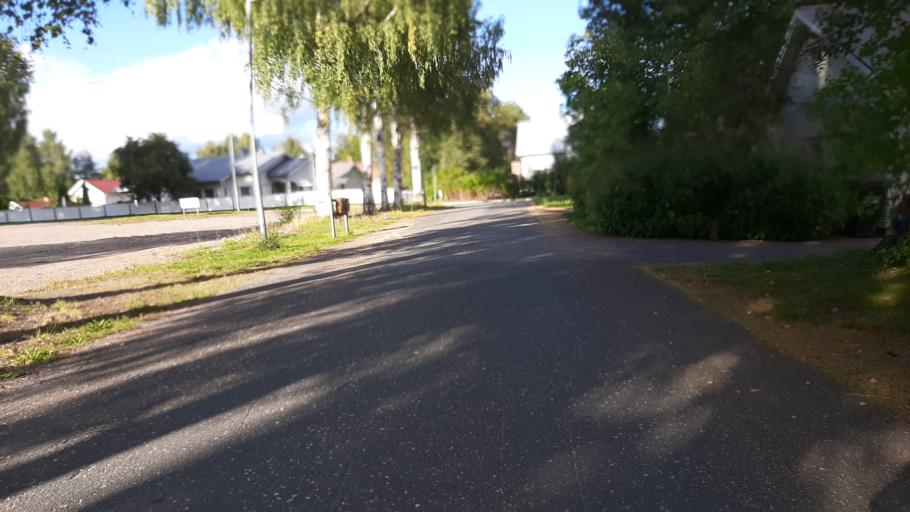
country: FI
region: North Karelia
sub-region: Joensuu
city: Joensuu
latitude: 62.6122
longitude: 29.7917
